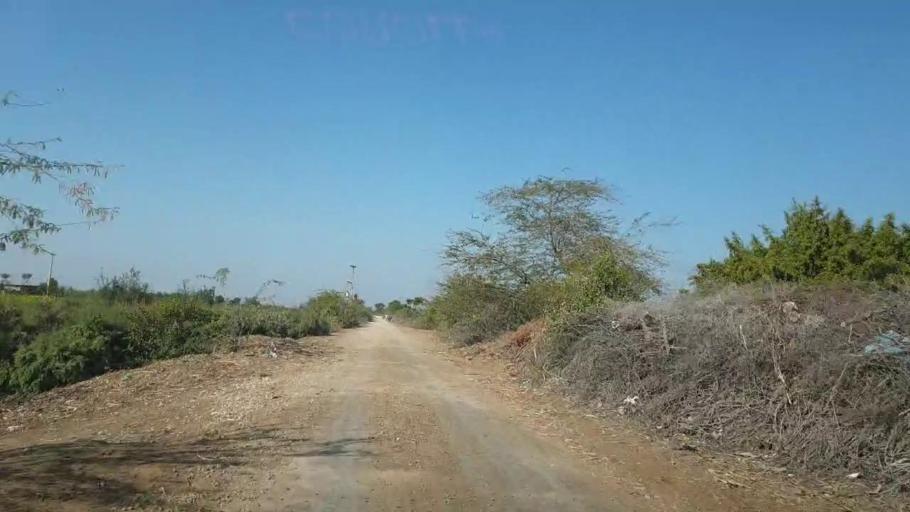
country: PK
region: Sindh
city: Mirpur Khas
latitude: 25.6403
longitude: 69.0586
